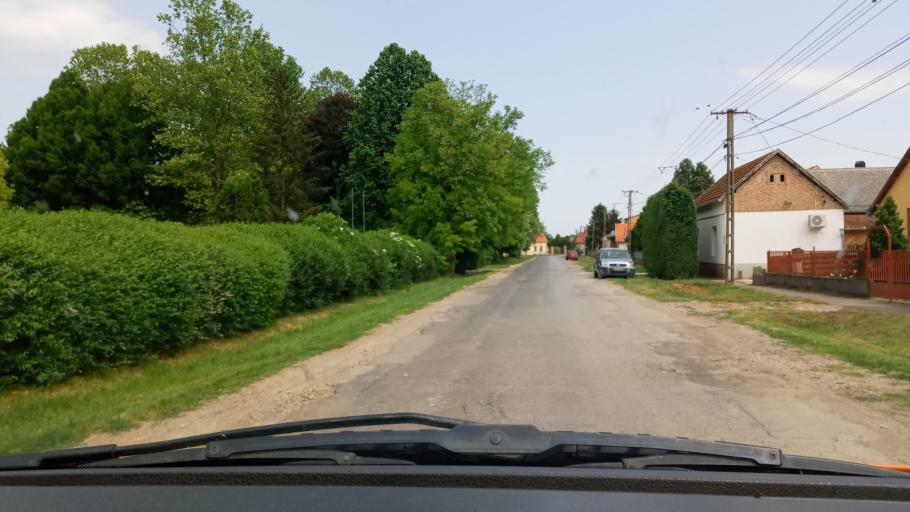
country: HU
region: Baranya
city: Szentlorinc
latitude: 46.0051
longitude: 18.0383
